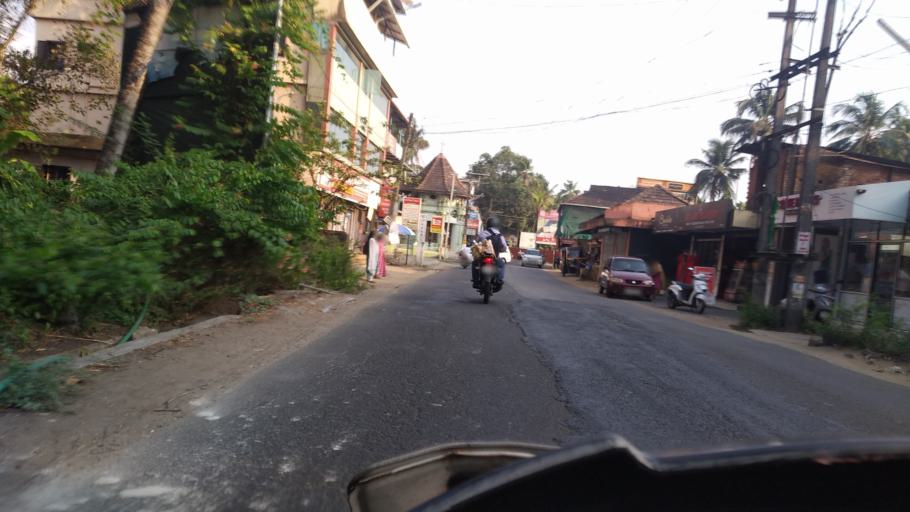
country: IN
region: Kerala
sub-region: Thrissur District
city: Thanniyam
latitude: 10.4004
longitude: 76.1132
